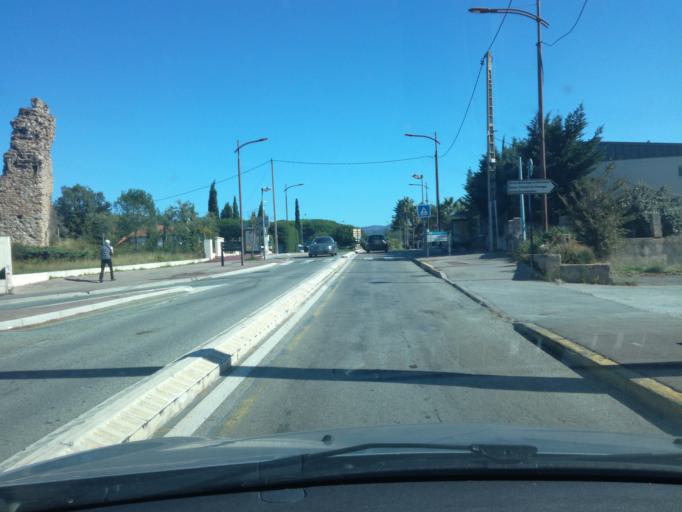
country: FR
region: Provence-Alpes-Cote d'Azur
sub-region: Departement du Var
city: Frejus
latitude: 43.4393
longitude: 6.7434
